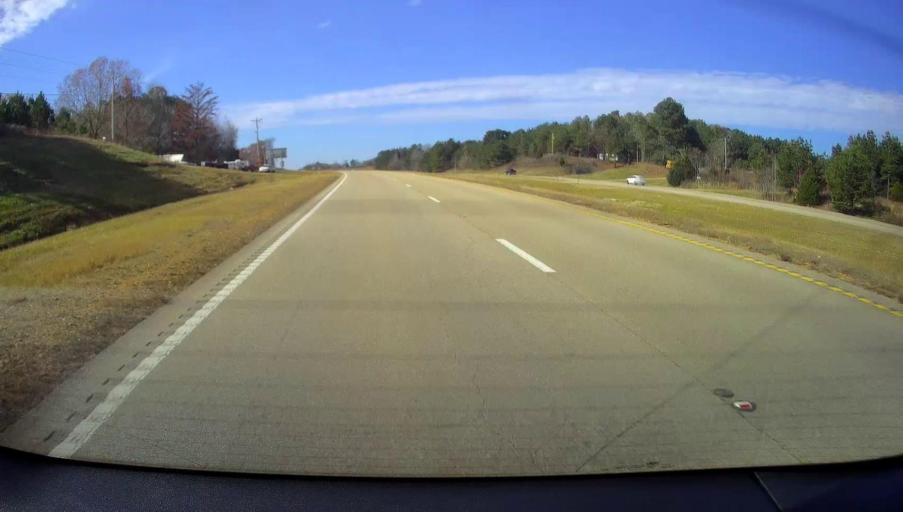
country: US
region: Mississippi
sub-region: Tippah County
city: Ripley
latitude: 34.9539
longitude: -88.9532
